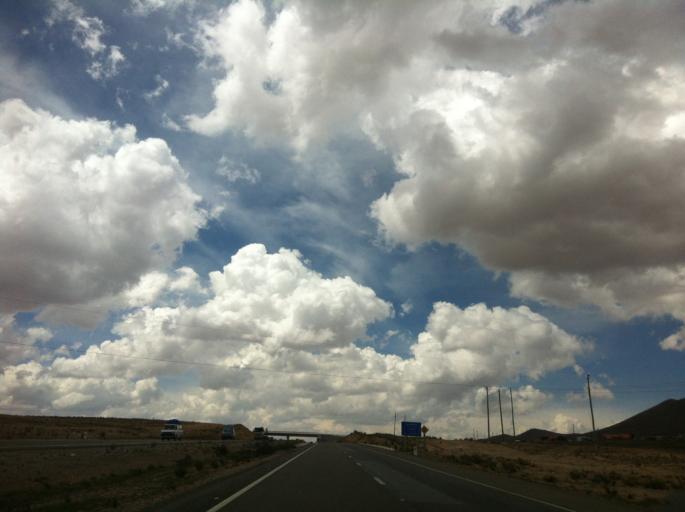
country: BO
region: La Paz
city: Patacamaya
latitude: -16.9174
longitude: -68.1155
